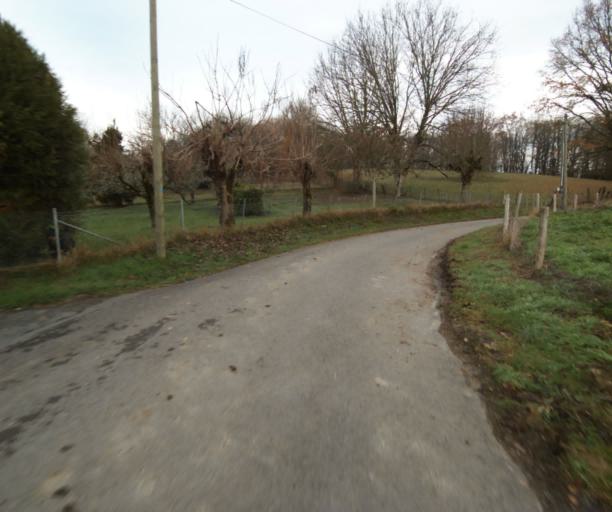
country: FR
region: Limousin
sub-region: Departement de la Correze
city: Chameyrat
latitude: 45.2286
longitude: 1.6978
